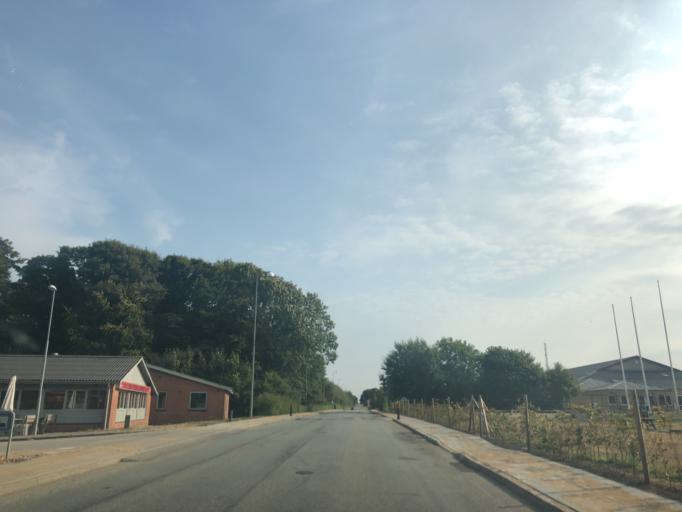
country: DK
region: Central Jutland
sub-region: Skive Kommune
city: Skive
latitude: 56.7018
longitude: 8.9807
